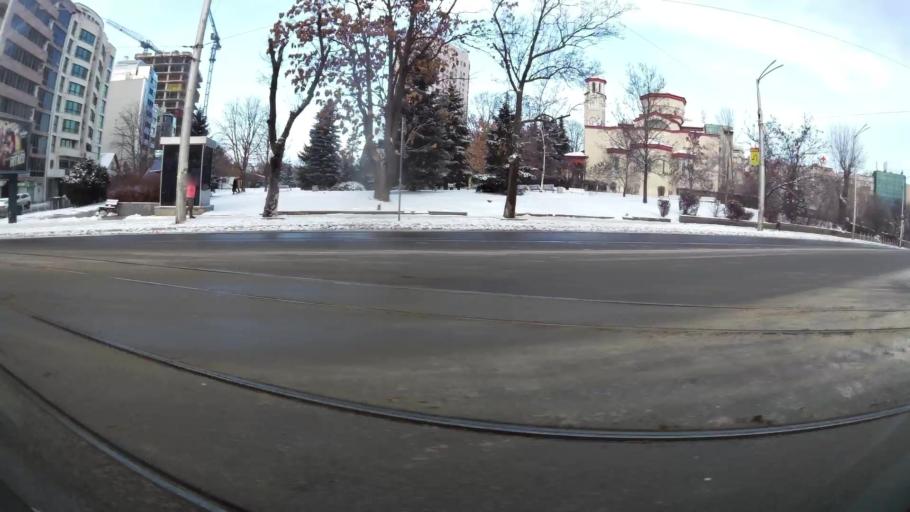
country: BG
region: Sofia-Capital
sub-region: Stolichna Obshtina
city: Sofia
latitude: 42.6712
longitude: 23.3211
